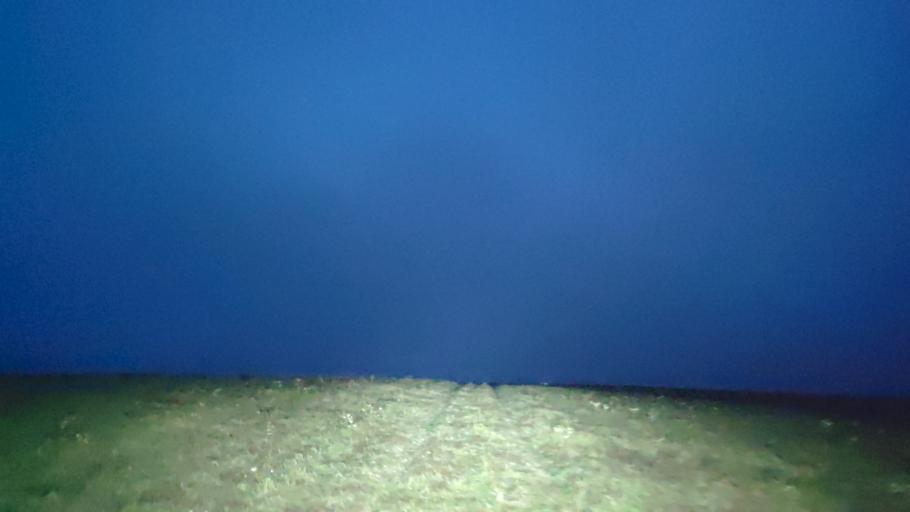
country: SK
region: Presovsky
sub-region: Okres Presov
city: Presov
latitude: 48.9353
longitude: 21.1181
